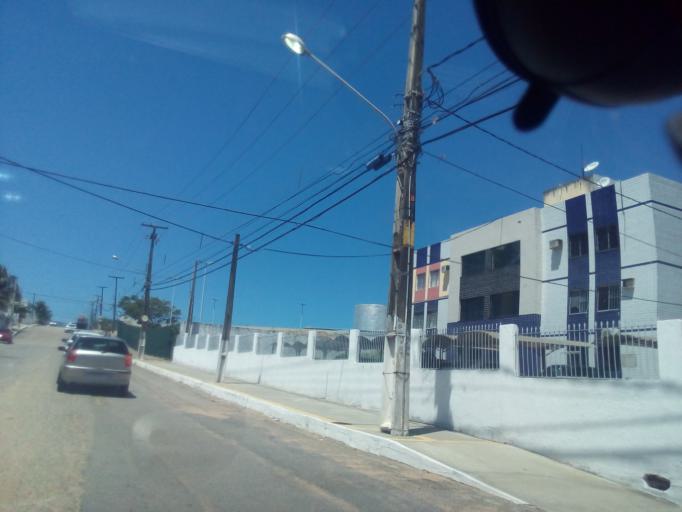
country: BR
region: Rio Grande do Norte
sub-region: Natal
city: Natal
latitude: -5.8460
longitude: -35.2124
